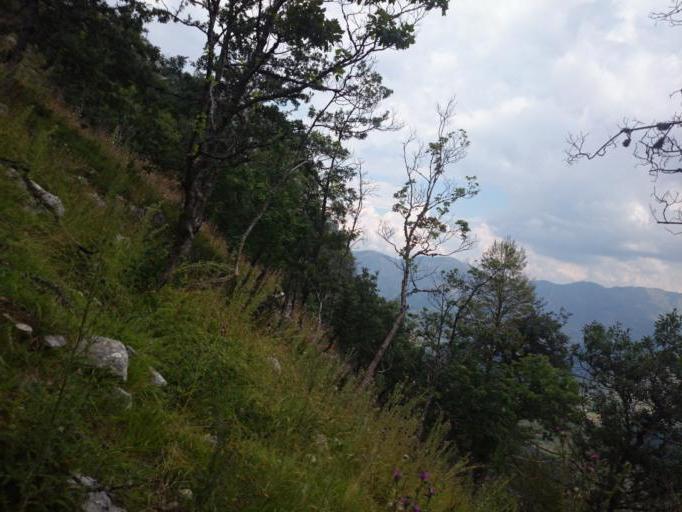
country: AL
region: Lezhe
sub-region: Rrethi i Mirdites
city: Orosh
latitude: 41.8434
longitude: 20.1552
